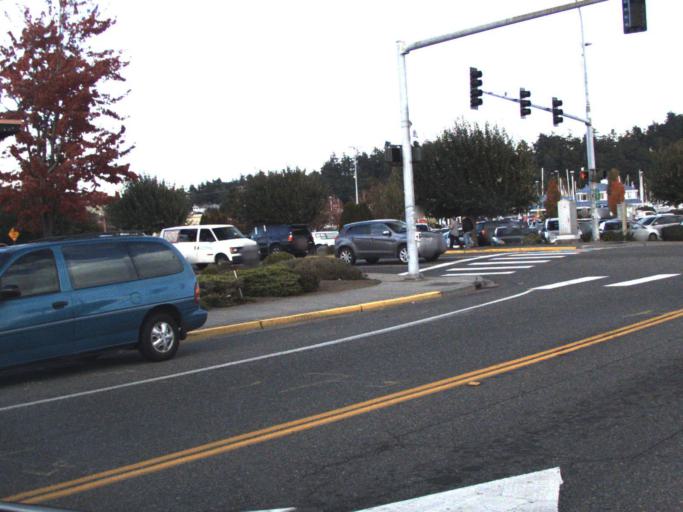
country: US
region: Washington
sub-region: Jefferson County
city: Port Hadlock-Irondale
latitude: 48.0187
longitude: -122.8306
